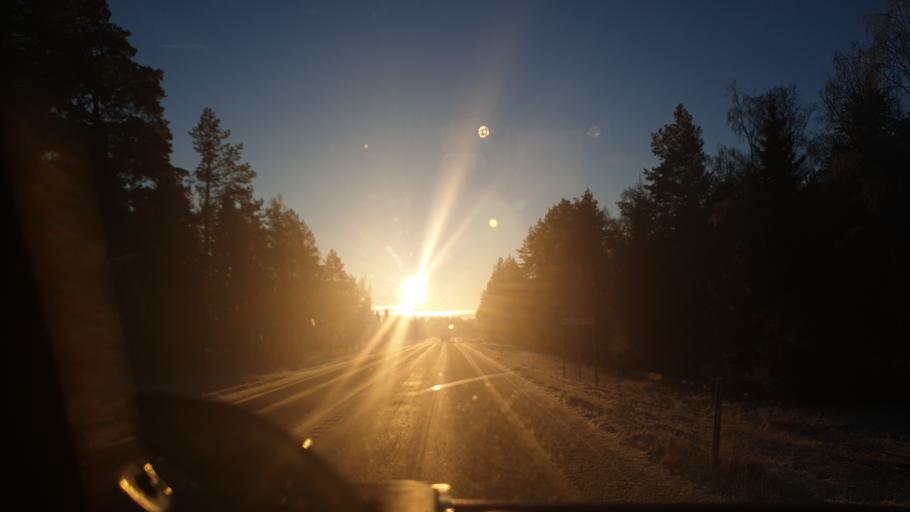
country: FI
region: Northern Ostrobothnia
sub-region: Ylivieska
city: Kalajoki
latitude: 64.2875
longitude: 23.9460
